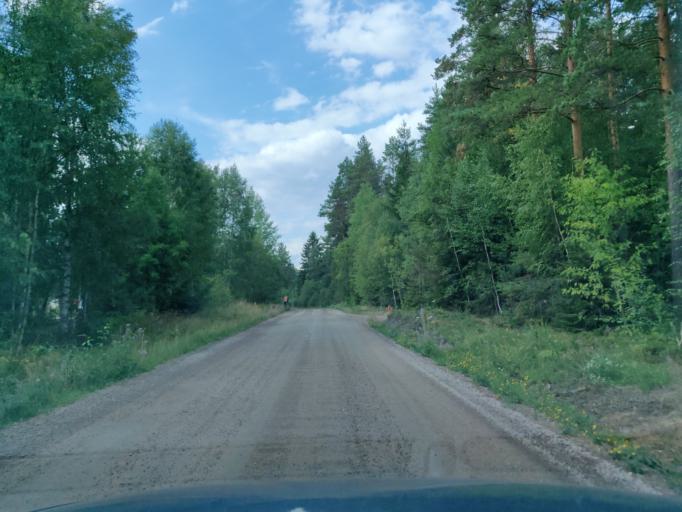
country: SE
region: Vaermland
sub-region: Munkfors Kommun
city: Munkfors
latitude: 59.9780
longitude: 13.5319
